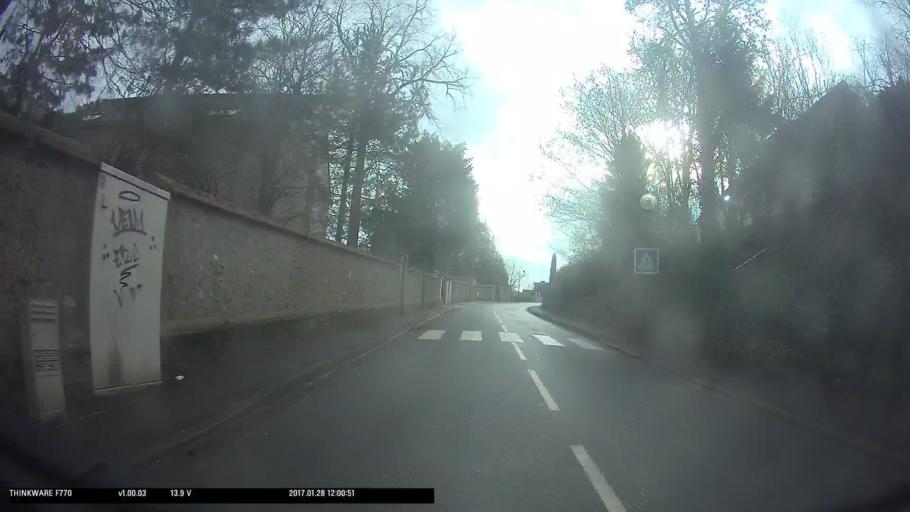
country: FR
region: Ile-de-France
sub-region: Departement du Val-d'Oise
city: Us
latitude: 49.1014
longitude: 1.9650
